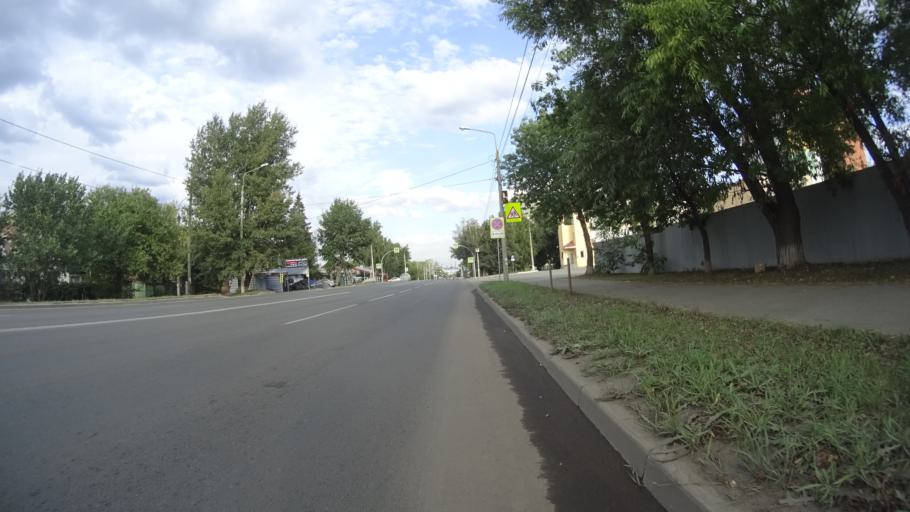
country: RU
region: Chelyabinsk
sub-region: Gorod Chelyabinsk
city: Chelyabinsk
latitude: 55.1984
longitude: 61.3584
